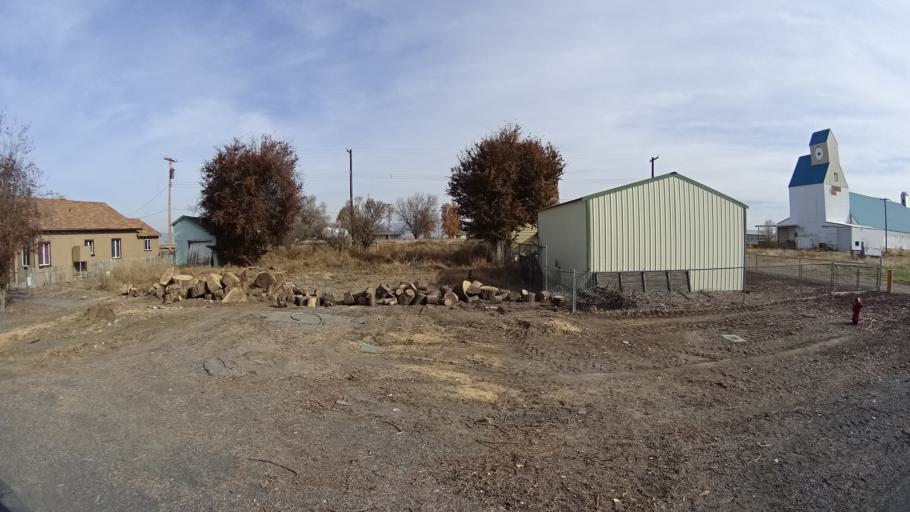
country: US
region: California
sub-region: Siskiyou County
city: Tulelake
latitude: 41.9593
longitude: -121.4782
